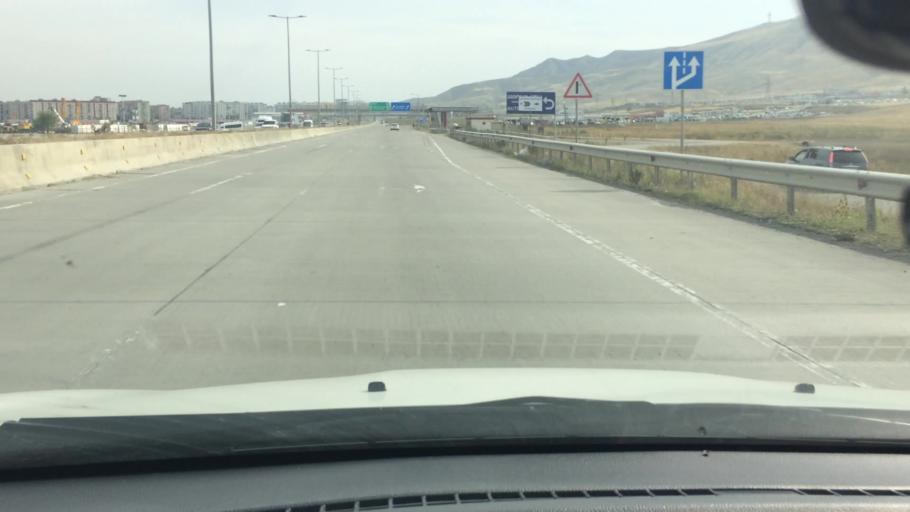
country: GE
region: Kvemo Kartli
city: Rust'avi
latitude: 41.5784
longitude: 44.9549
